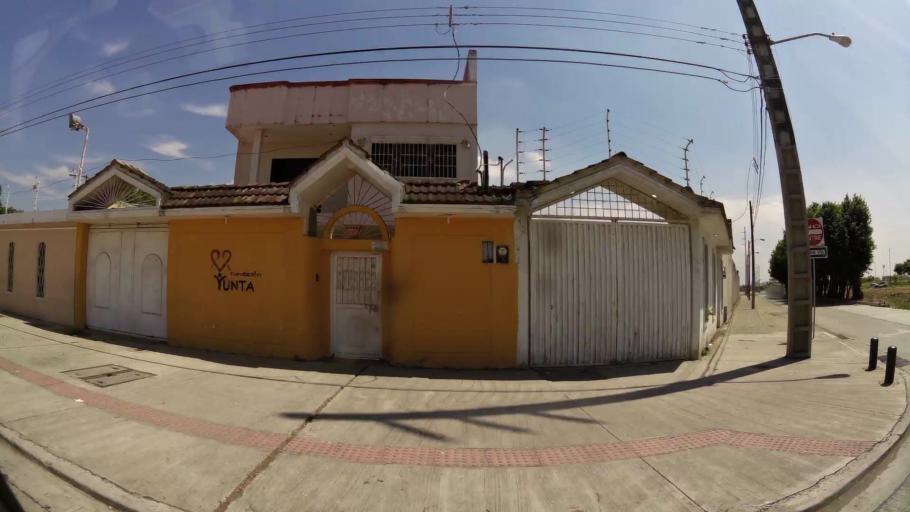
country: EC
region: Guayas
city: Eloy Alfaro
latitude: -2.1078
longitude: -79.8991
